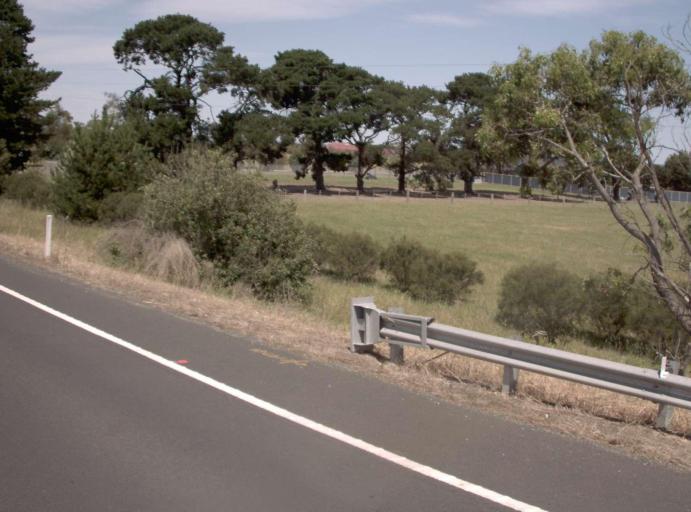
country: AU
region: Victoria
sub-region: Wellington
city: Sale
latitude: -38.1059
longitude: 146.9070
